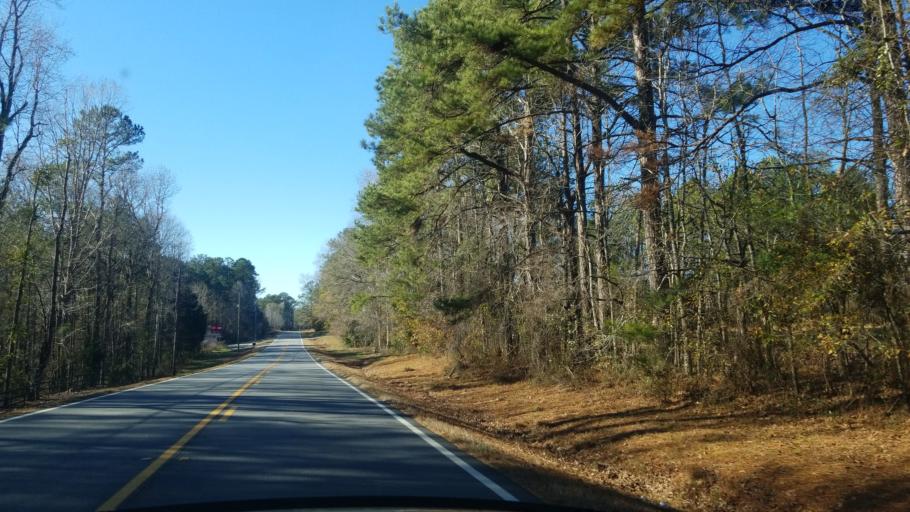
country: US
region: Georgia
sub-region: Harris County
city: Hamilton
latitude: 32.6673
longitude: -84.8915
